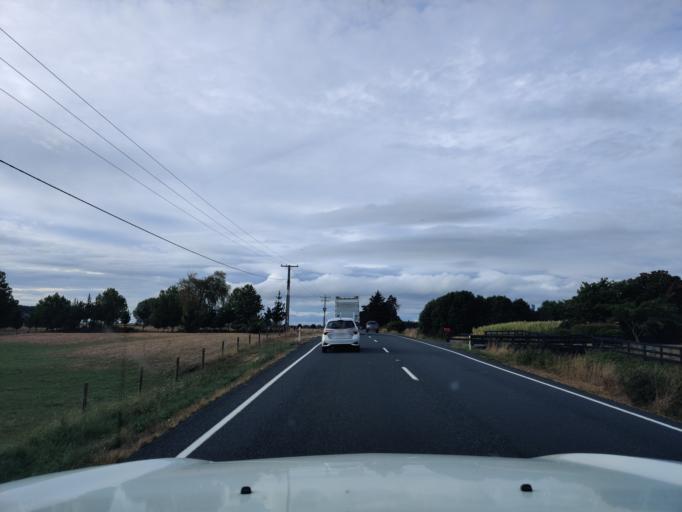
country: NZ
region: Waikato
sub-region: Hamilton City
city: Hamilton
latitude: -37.7024
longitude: 175.3381
